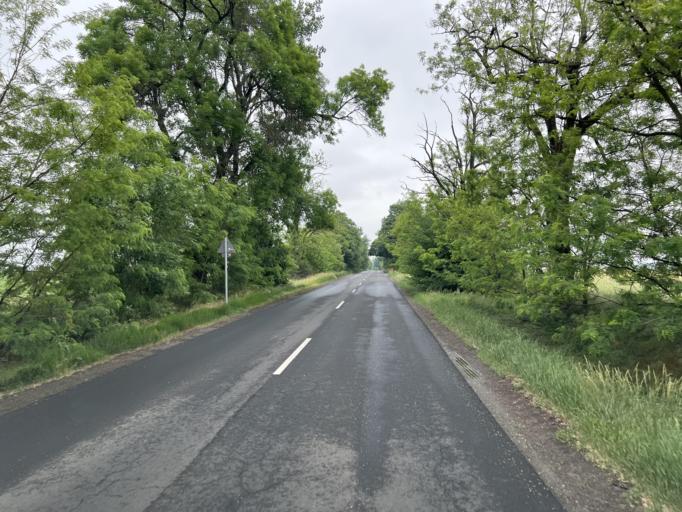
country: HU
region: Pest
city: Zsambok
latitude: 47.5650
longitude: 19.6030
